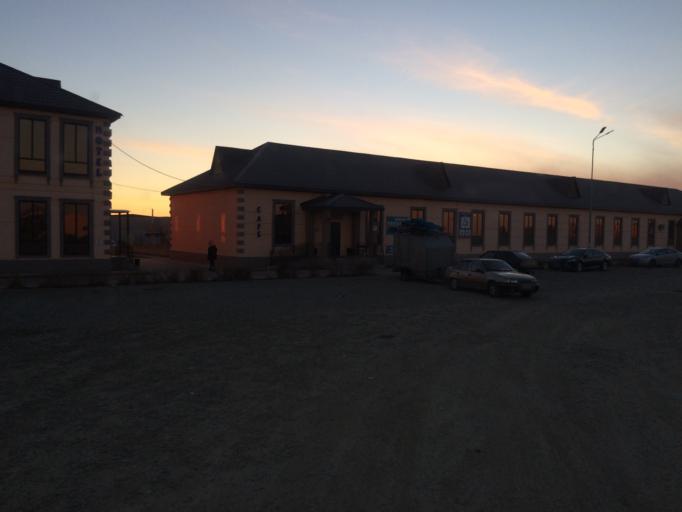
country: RU
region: Orenburg
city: Dombarovskiy
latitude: 49.9689
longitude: 60.0639
